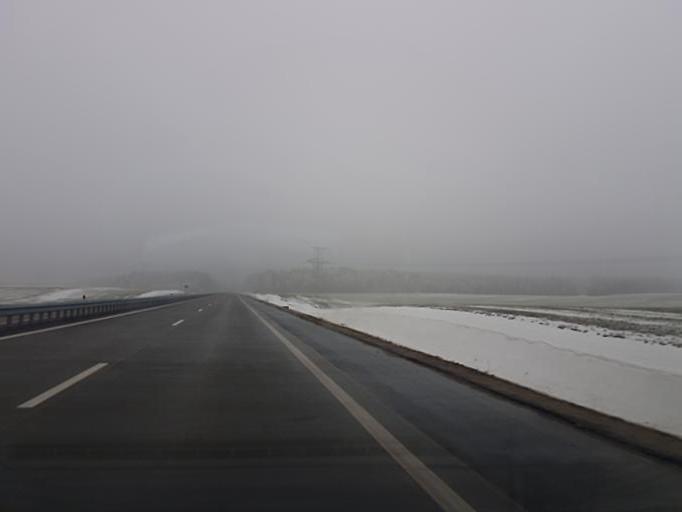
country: BY
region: Minsk
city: Atolina
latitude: 53.7137
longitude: 27.4365
